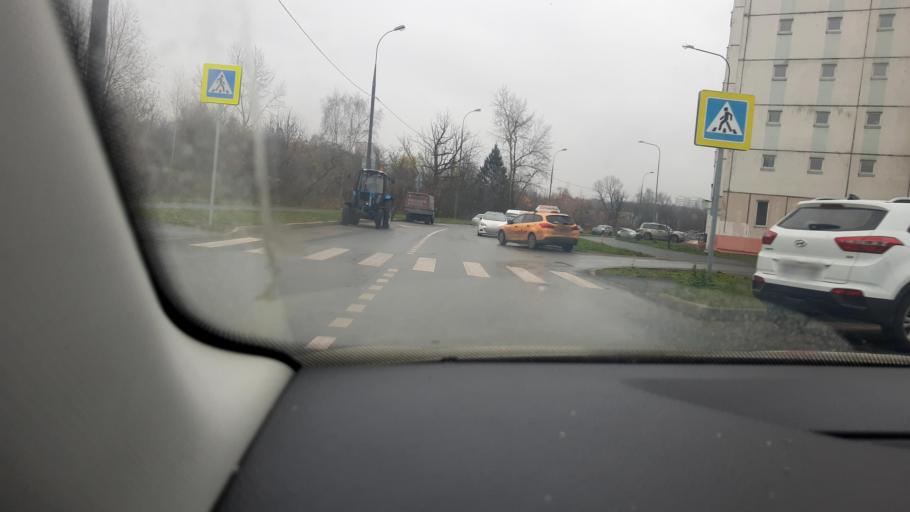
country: RU
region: Moscow
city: Annino
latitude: 55.5521
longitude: 37.5716
